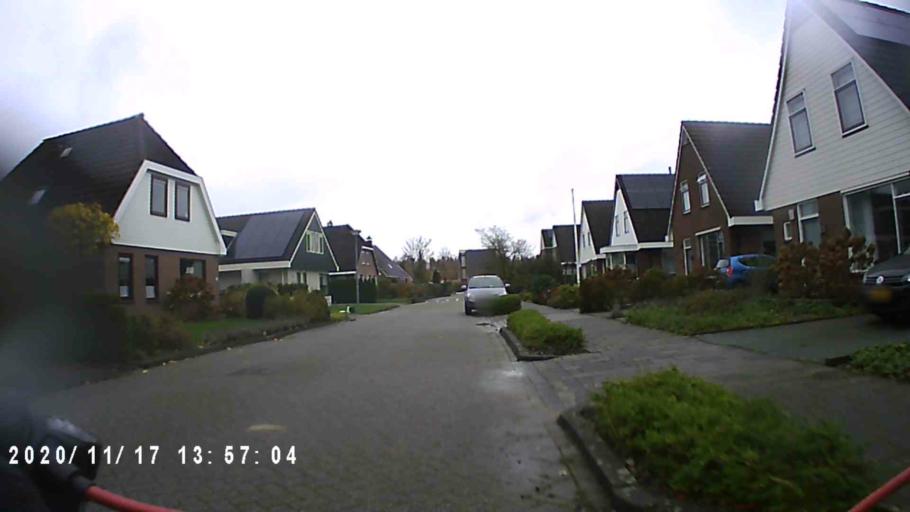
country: NL
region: Groningen
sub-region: Gemeente Zuidhorn
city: Grijpskerk
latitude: 53.2223
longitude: 6.3484
